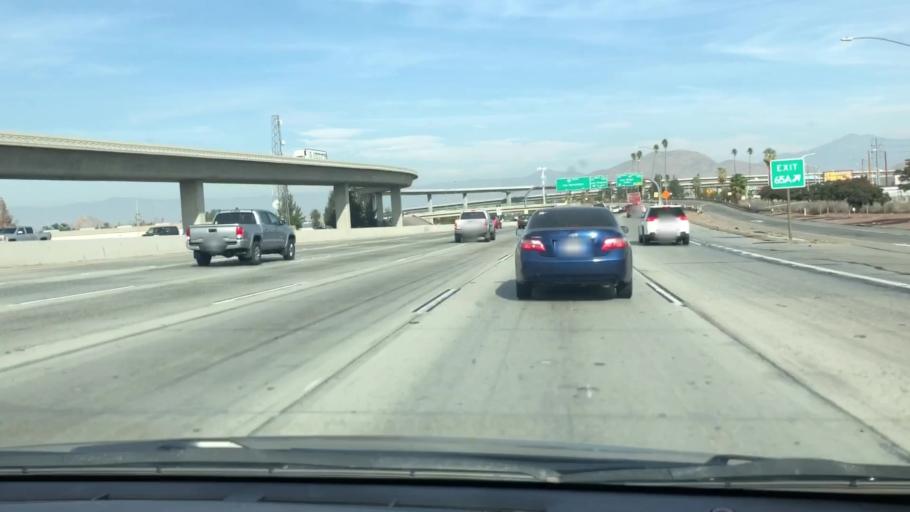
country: US
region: California
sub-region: Riverside County
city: Highgrove
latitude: 33.9882
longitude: -117.3621
